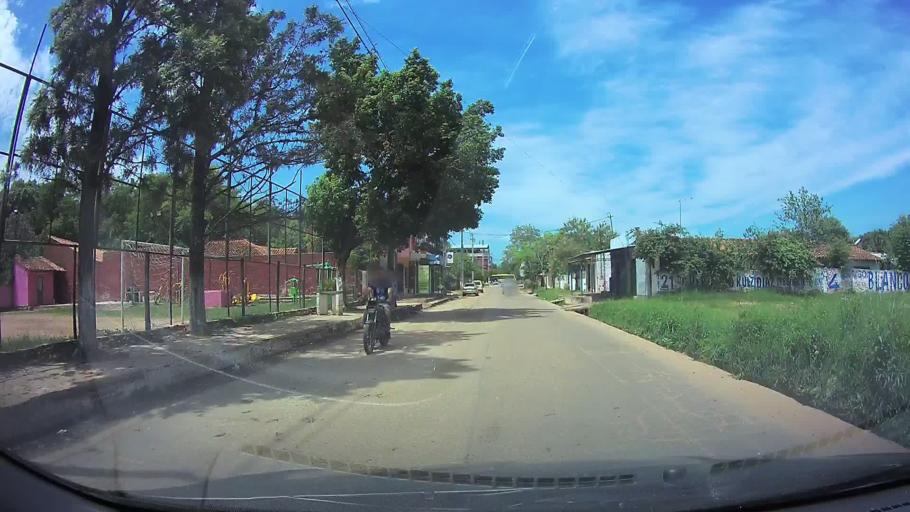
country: PY
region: Central
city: Limpio
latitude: -25.1715
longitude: -57.4753
